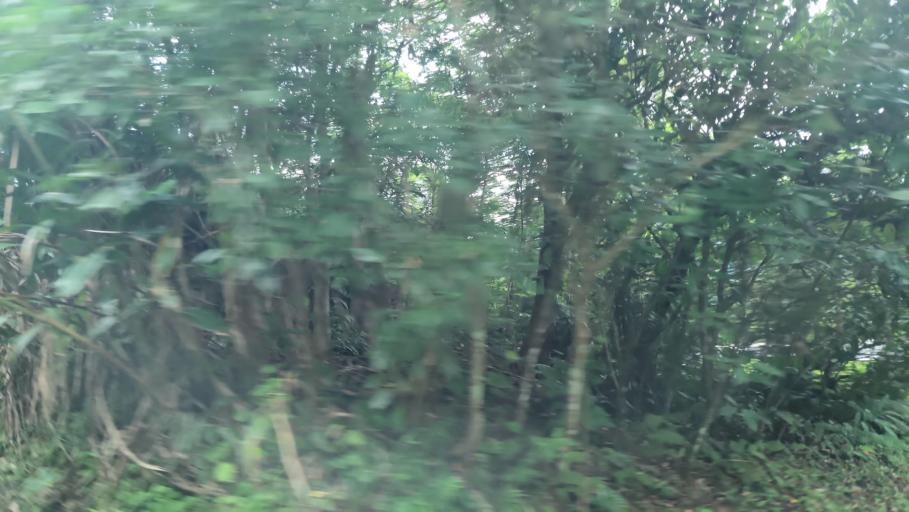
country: TW
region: Taipei
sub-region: Taipei
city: Banqiao
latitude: 24.8914
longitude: 121.4289
